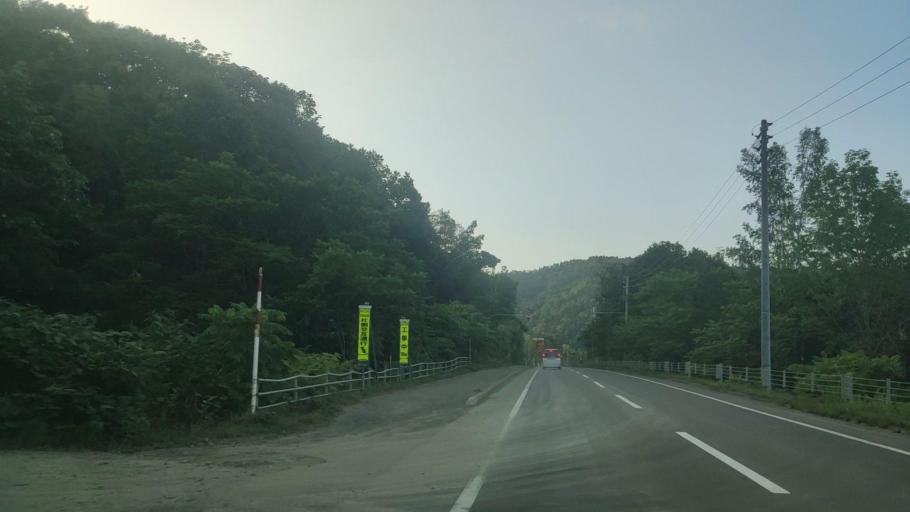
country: JP
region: Hokkaido
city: Bibai
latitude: 43.2302
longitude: 142.0399
